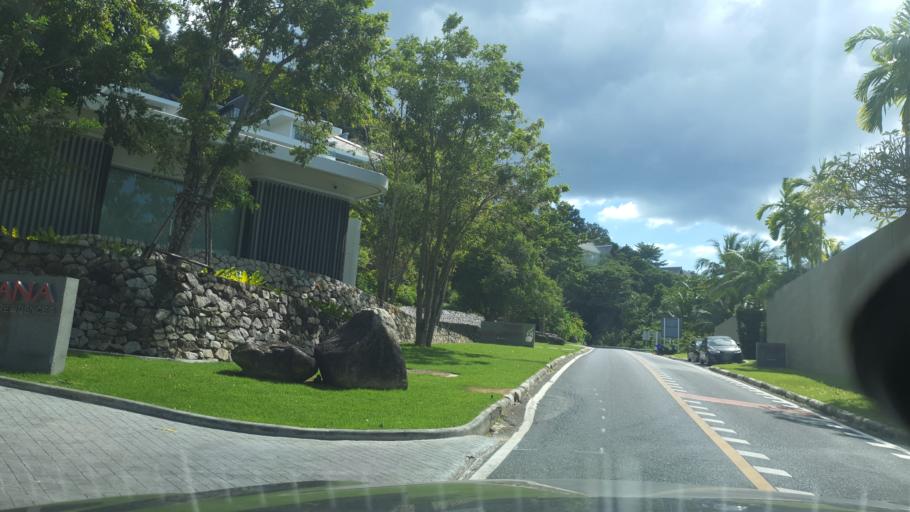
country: TH
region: Phuket
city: Thalang
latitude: 8.0551
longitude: 98.2786
